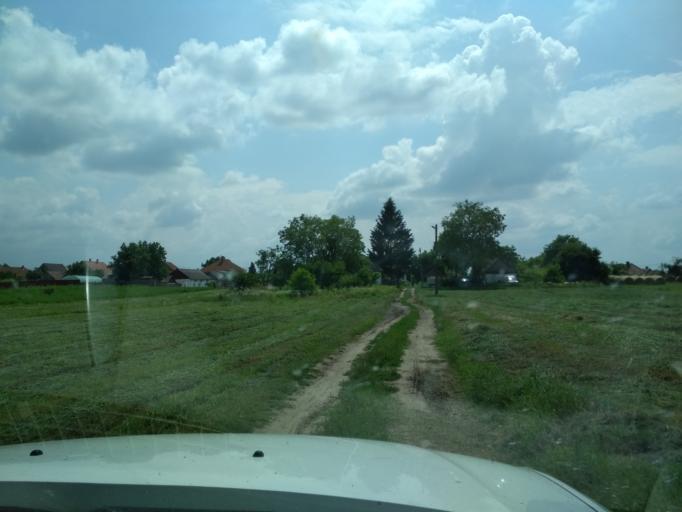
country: HU
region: Pest
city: Tapioszentmarton
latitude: 47.3471
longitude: 19.7422
